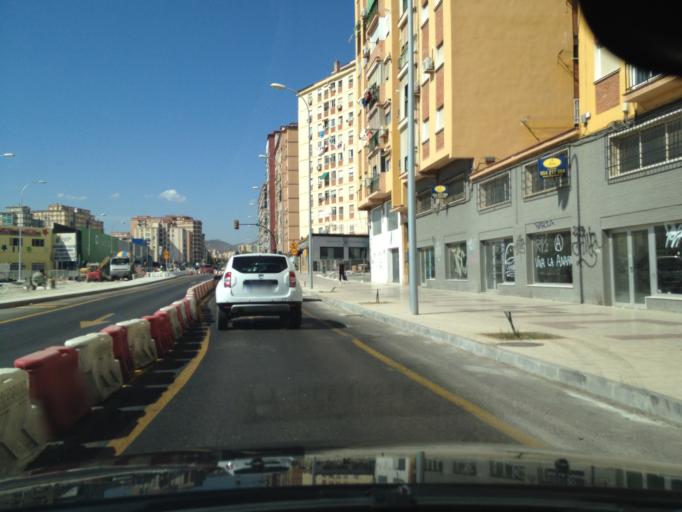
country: ES
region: Andalusia
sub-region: Provincia de Malaga
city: Malaga
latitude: 36.7070
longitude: -4.4429
